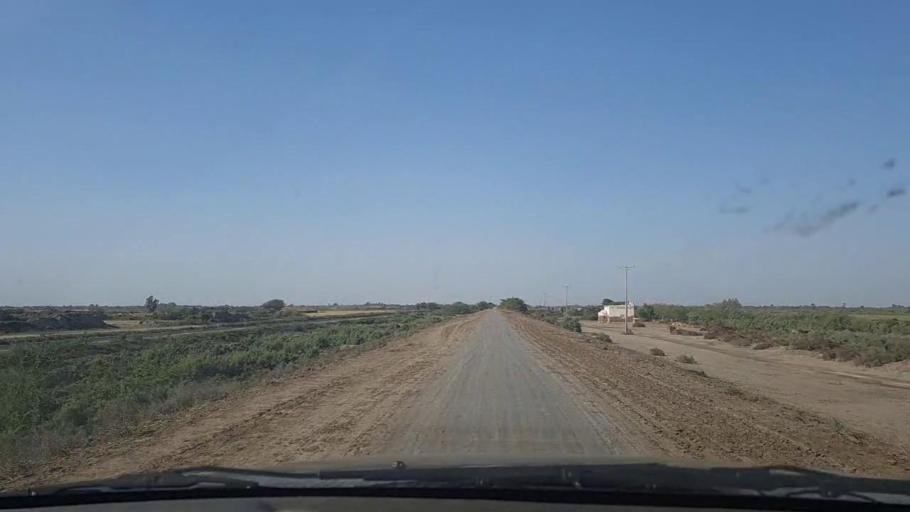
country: PK
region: Sindh
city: Chuhar Jamali
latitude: 24.3027
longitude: 67.7548
